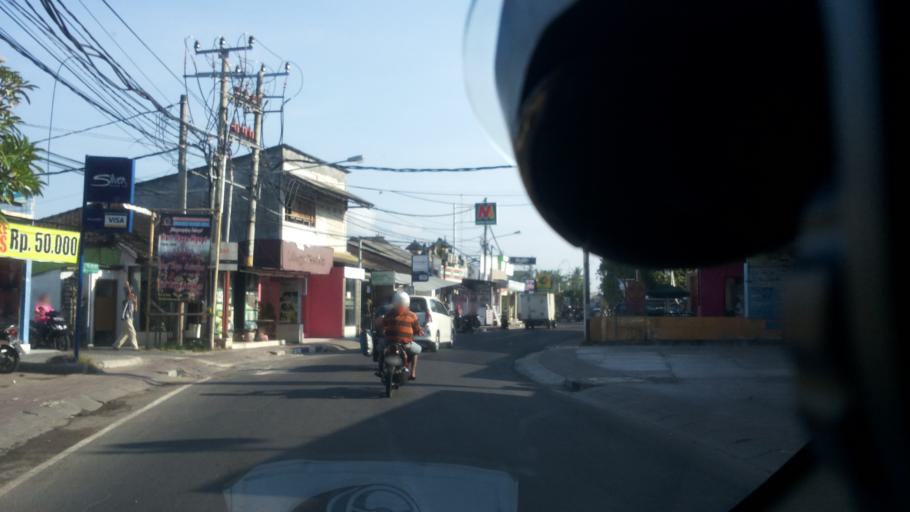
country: ID
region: Bali
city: Bualu
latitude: -8.7696
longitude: 115.2221
